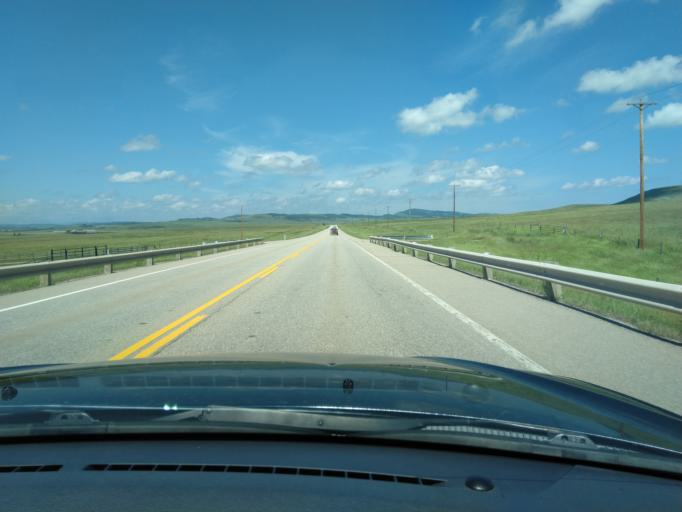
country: CA
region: Alberta
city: Cochrane
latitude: 51.2219
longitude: -114.5466
